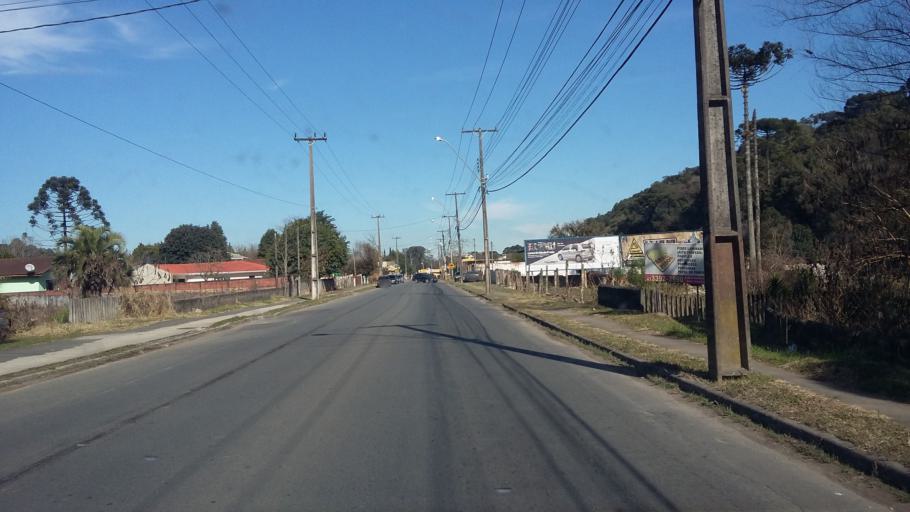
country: BR
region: Parana
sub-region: Campo Largo
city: Campo Largo
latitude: -25.4652
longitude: -49.5628
